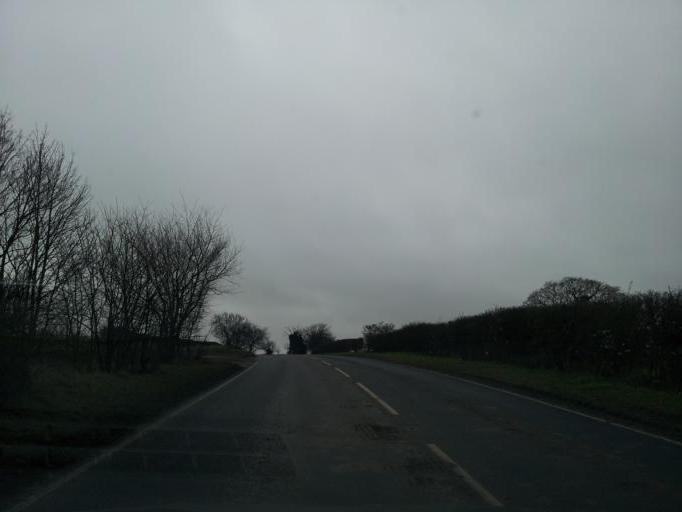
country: GB
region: England
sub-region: Essex
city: Mistley
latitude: 51.9314
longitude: 1.0777
